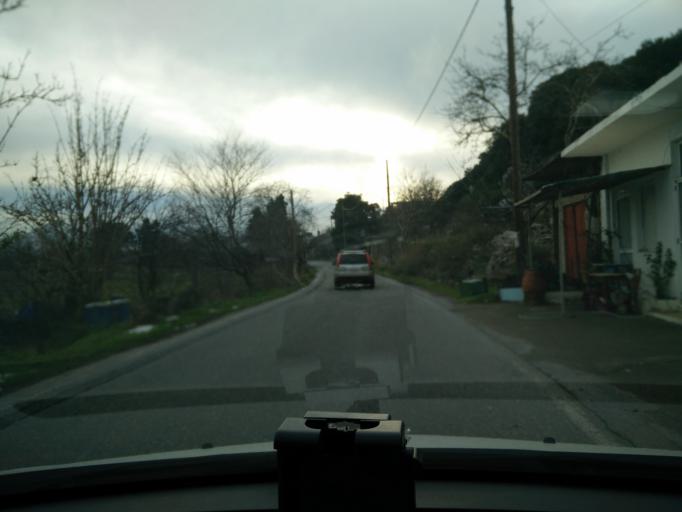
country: GR
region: Crete
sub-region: Nomos Irakleiou
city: Mokhos
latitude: 35.2025
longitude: 25.4734
